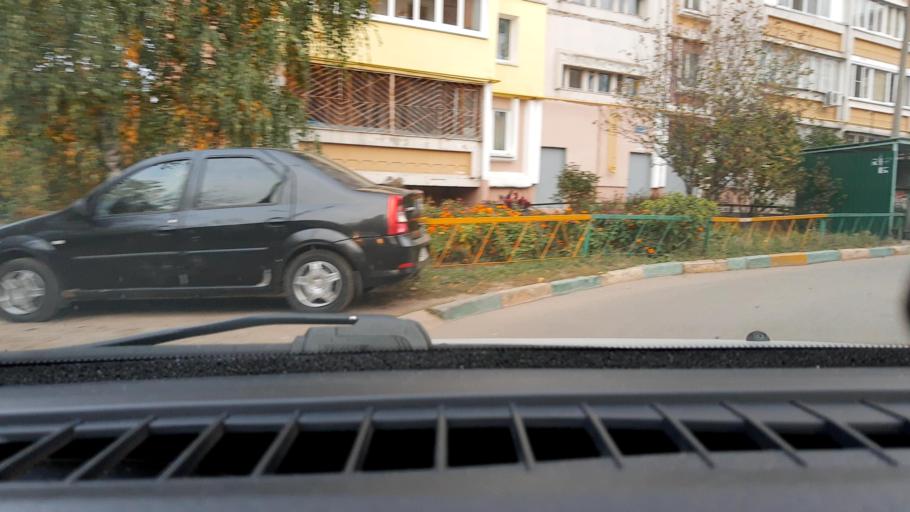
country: RU
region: Nizjnij Novgorod
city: Gorbatovka
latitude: 56.3660
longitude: 43.8013
